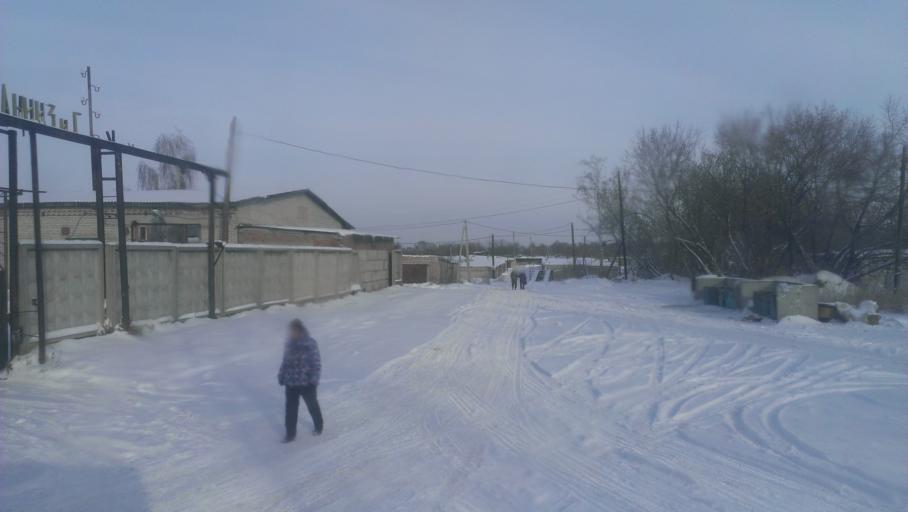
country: RU
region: Altai Krai
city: Nauchnyy Gorodok
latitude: 53.4211
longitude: 83.5223
